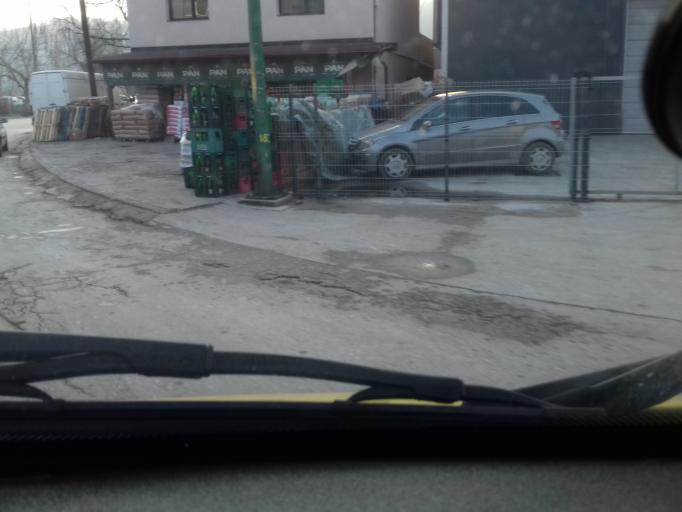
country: BA
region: Federation of Bosnia and Herzegovina
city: Kakanj
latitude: 44.1219
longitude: 18.1068
